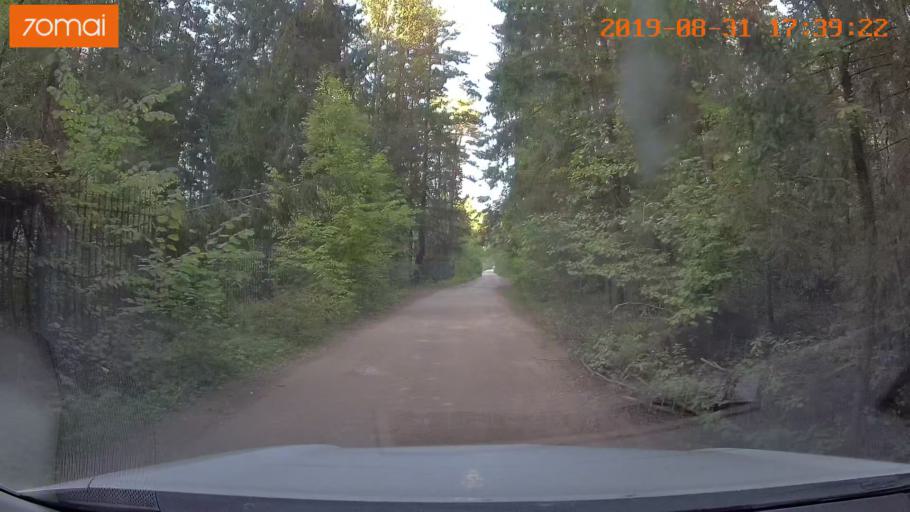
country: RU
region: Kaluga
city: Detchino
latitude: 54.8173
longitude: 36.3631
